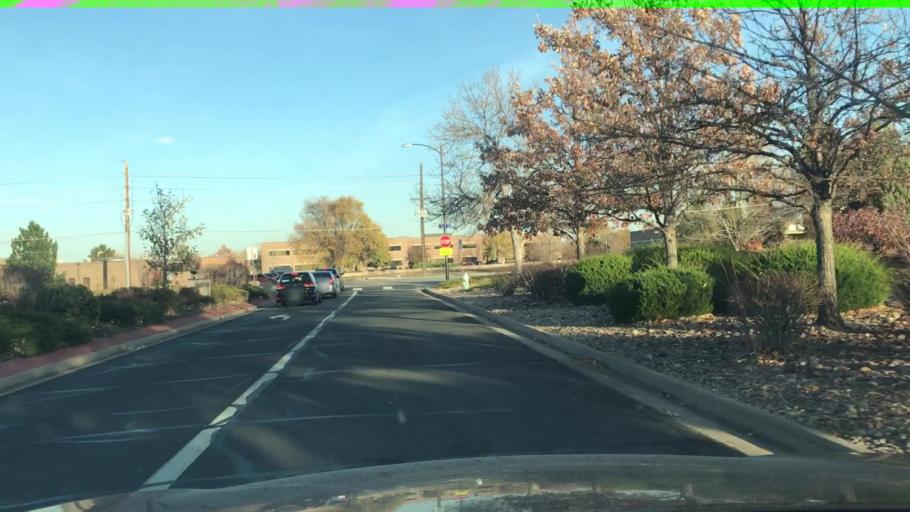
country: US
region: Colorado
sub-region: Boulder County
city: Gunbarrel
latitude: 40.0642
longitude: -105.2076
